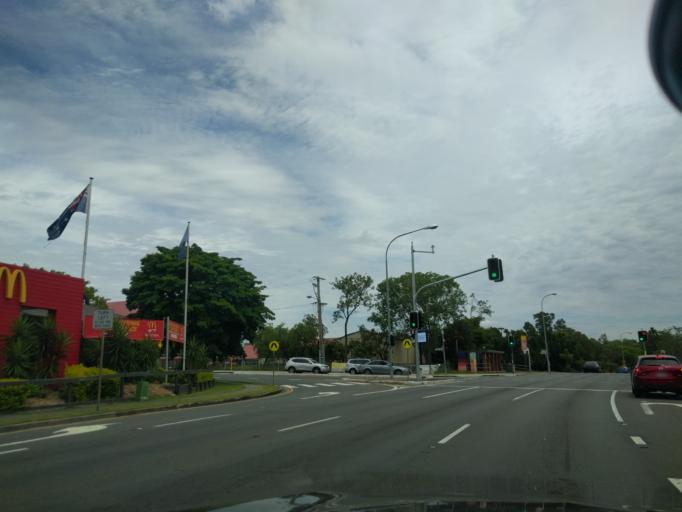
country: AU
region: Queensland
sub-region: Brisbane
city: Wilston
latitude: -27.4325
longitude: 153.0051
